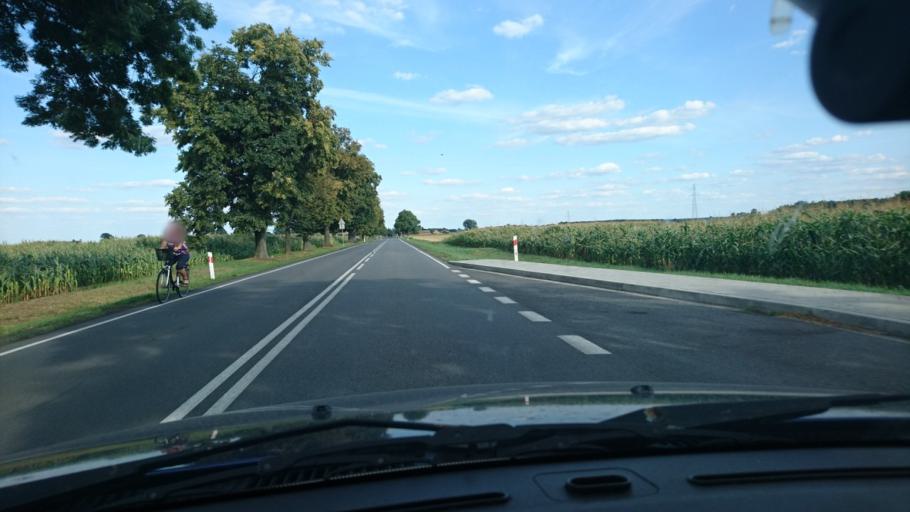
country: PL
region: Greater Poland Voivodeship
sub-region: Powiat krotoszynski
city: Zduny
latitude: 51.7210
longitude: 17.3533
